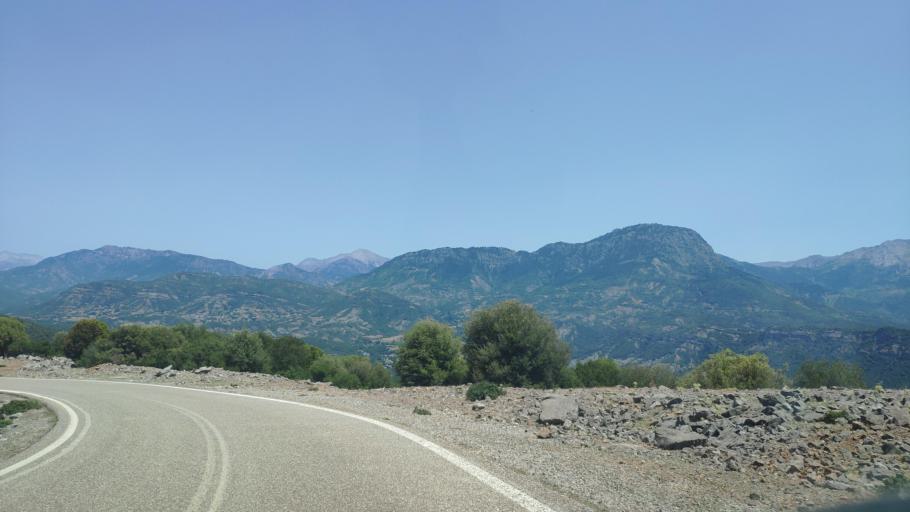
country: GR
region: Central Greece
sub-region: Nomos Evrytanias
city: Kerasochori
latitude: 39.0867
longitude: 21.4138
